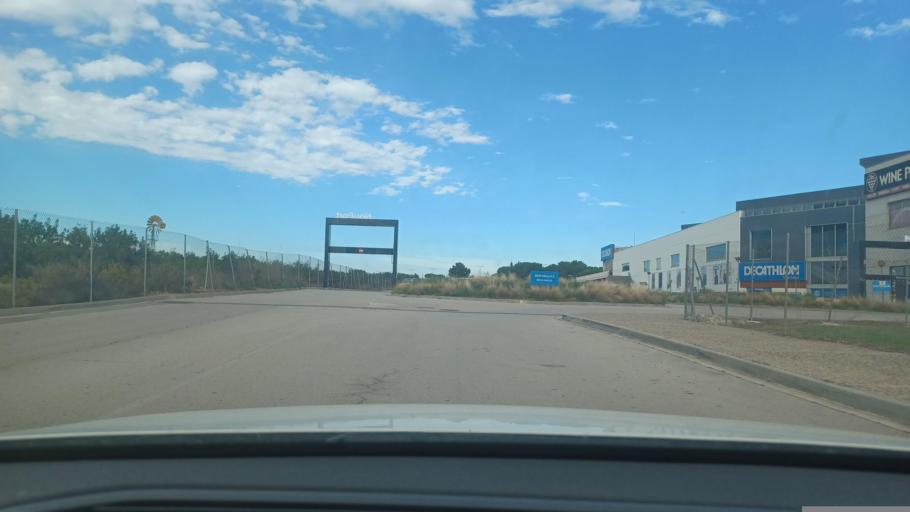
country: ES
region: Catalonia
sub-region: Provincia de Tarragona
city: Salou
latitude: 41.0957
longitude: 1.1500
